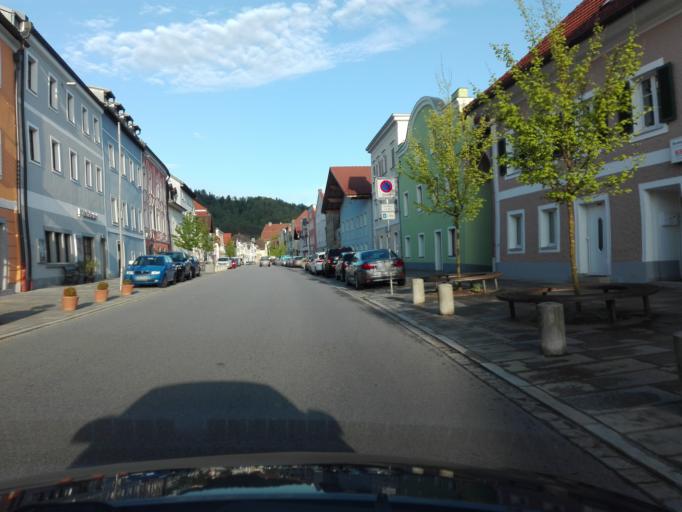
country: DE
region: Bavaria
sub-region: Lower Bavaria
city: Obernzell
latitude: 48.5546
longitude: 13.6361
